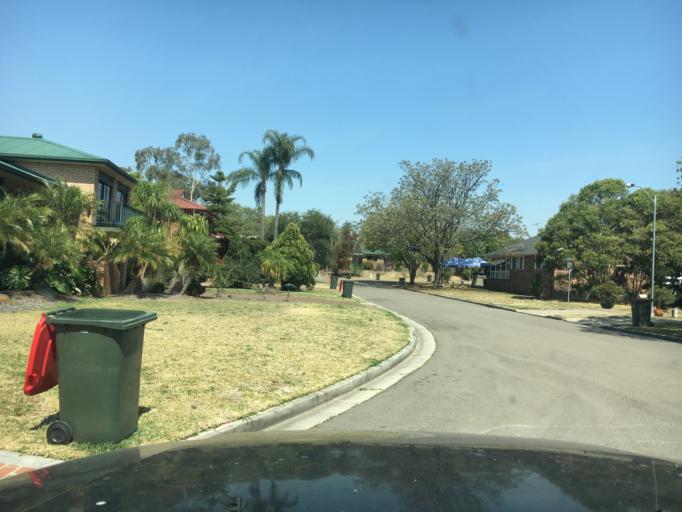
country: AU
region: New South Wales
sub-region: Singleton
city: Singleton
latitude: -32.5675
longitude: 151.1896
